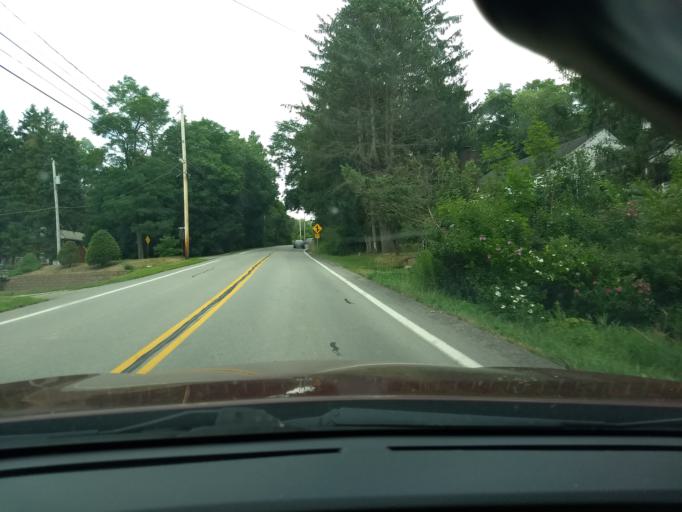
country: US
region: Pennsylvania
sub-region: Allegheny County
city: Bakerstown
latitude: 40.6521
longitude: -79.9230
